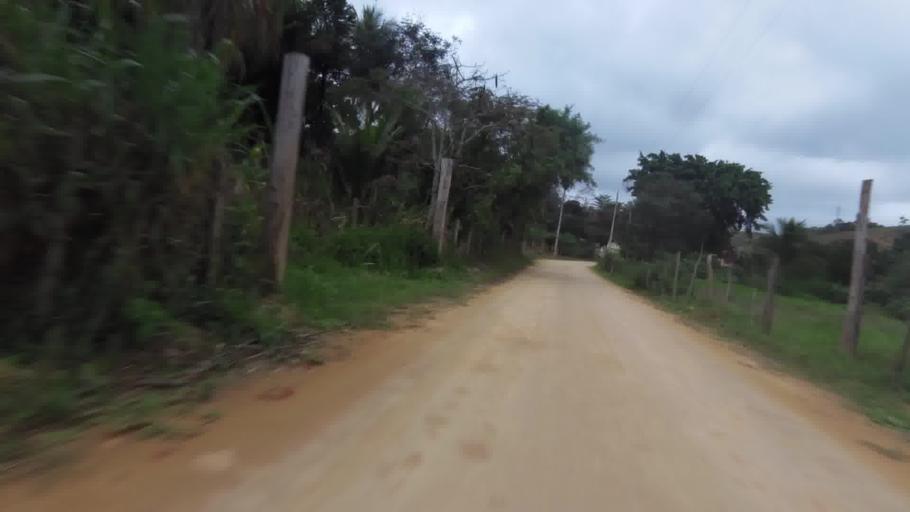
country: BR
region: Espirito Santo
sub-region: Alfredo Chaves
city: Alfredo Chaves
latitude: -20.6967
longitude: -40.7137
